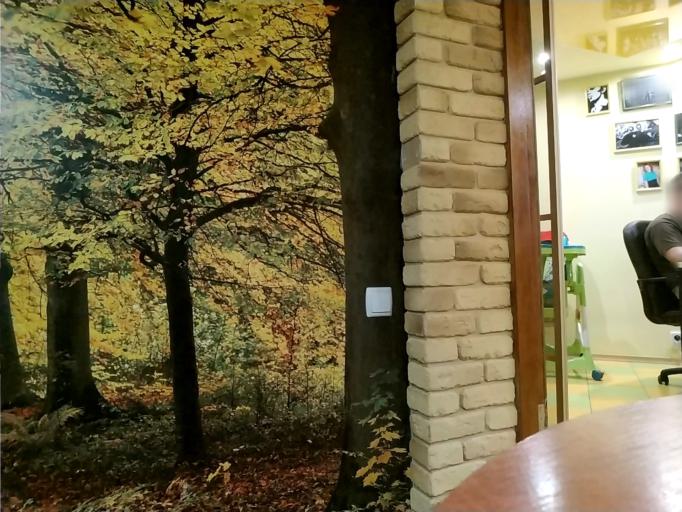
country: RU
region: Tverskaya
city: Zapadnaya Dvina
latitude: 56.3306
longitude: 31.8891
